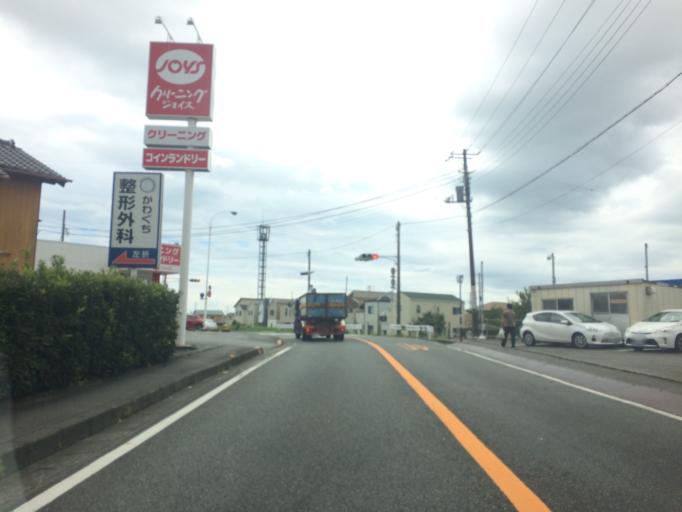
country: JP
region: Shizuoka
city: Fuji
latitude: 35.1450
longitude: 138.6468
